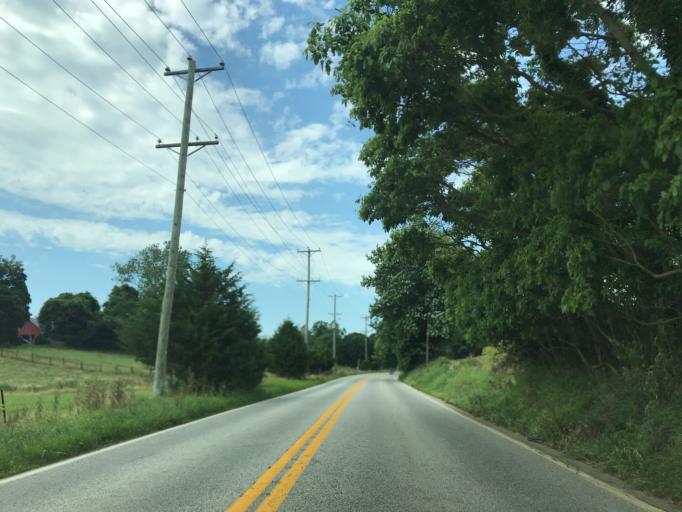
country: US
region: Maryland
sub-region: Harford County
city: Jarrettsville
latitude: 39.6587
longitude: -76.4075
